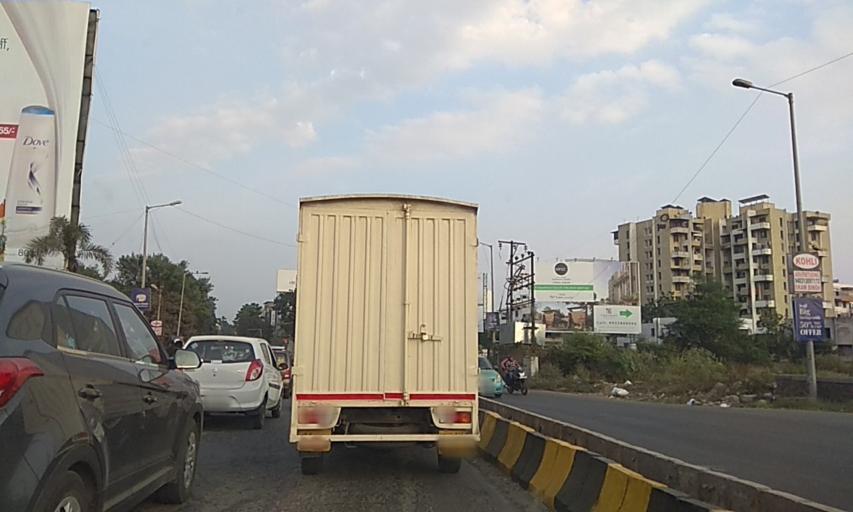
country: IN
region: Maharashtra
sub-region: Pune Division
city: Pimpri
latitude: 18.5888
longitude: 73.7778
